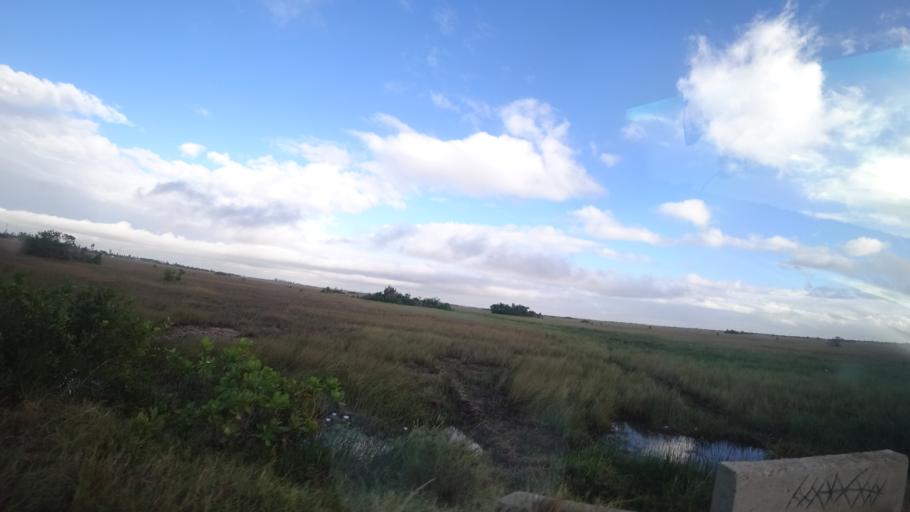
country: MZ
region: Sofala
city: Beira
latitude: -19.7083
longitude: 35.0174
